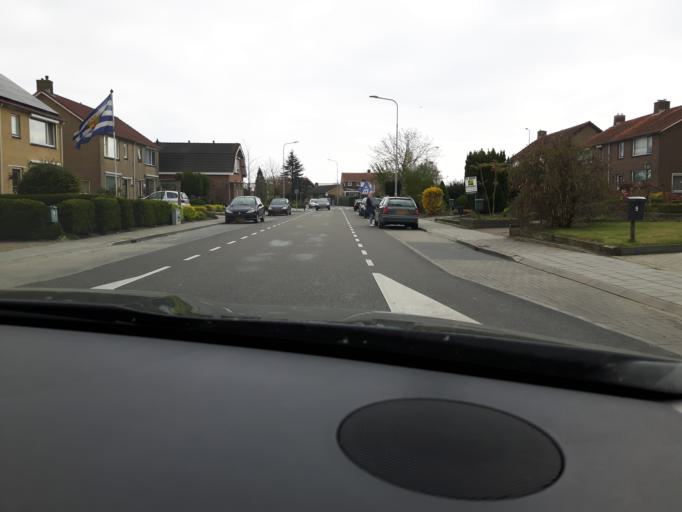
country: NL
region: Zeeland
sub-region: Gemeente Goes
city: Goes
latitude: 51.4759
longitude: 3.9646
